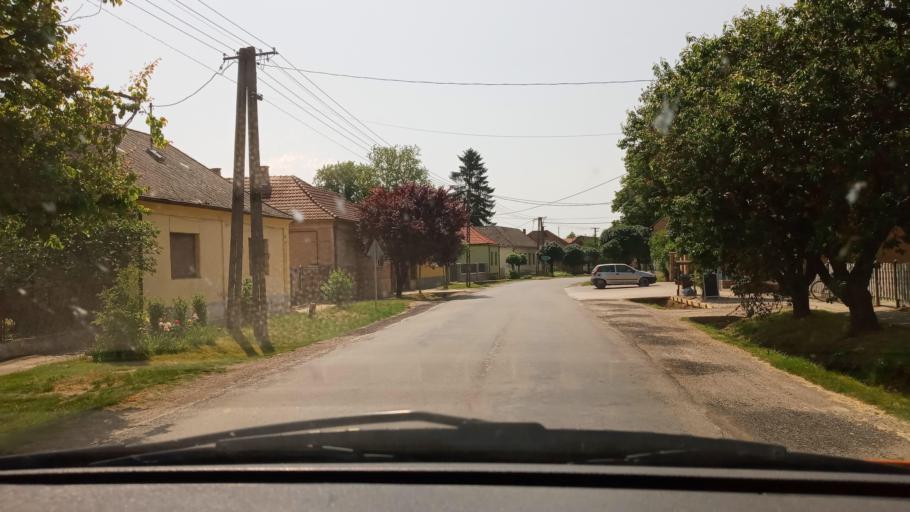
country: HU
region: Baranya
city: Szentlorinc
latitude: 46.0089
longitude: 18.0422
